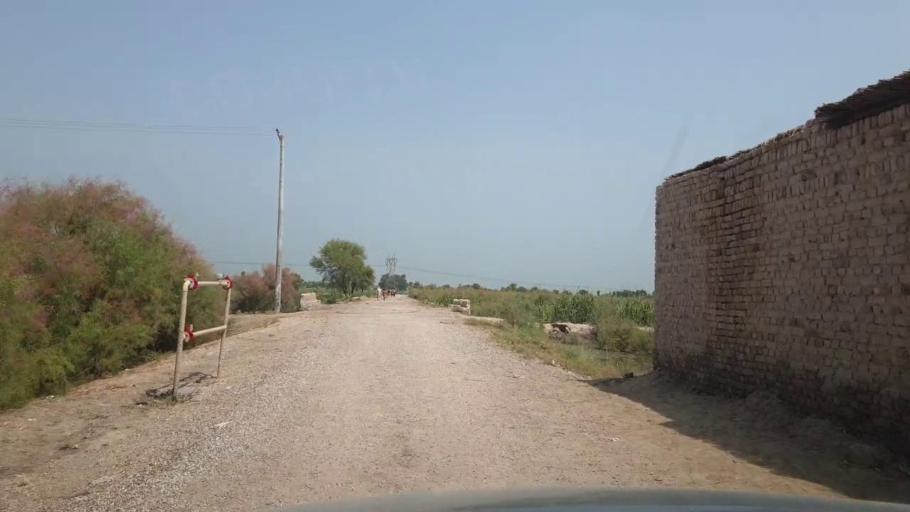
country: PK
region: Sindh
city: Madeji
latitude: 27.8009
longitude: 68.5209
